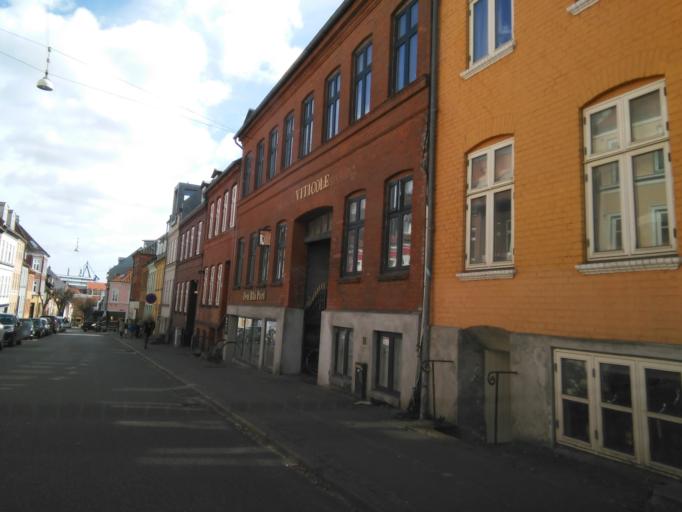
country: DK
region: Central Jutland
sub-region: Arhus Kommune
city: Arhus
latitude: 56.1624
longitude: 10.2067
